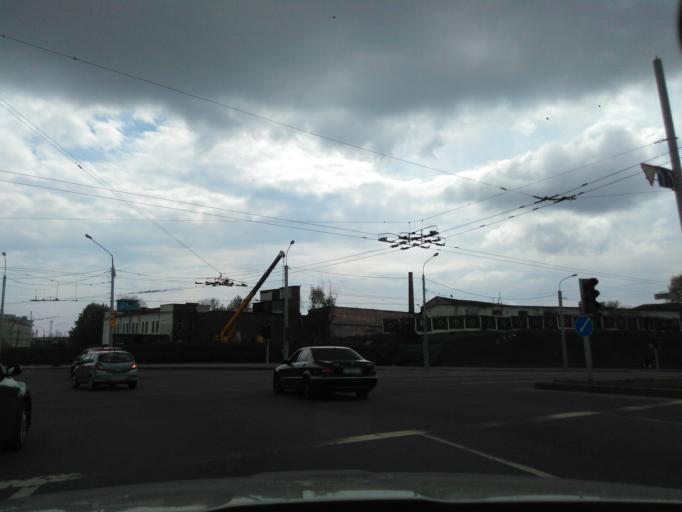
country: BY
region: Minsk
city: Minsk
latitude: 53.8964
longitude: 27.5373
